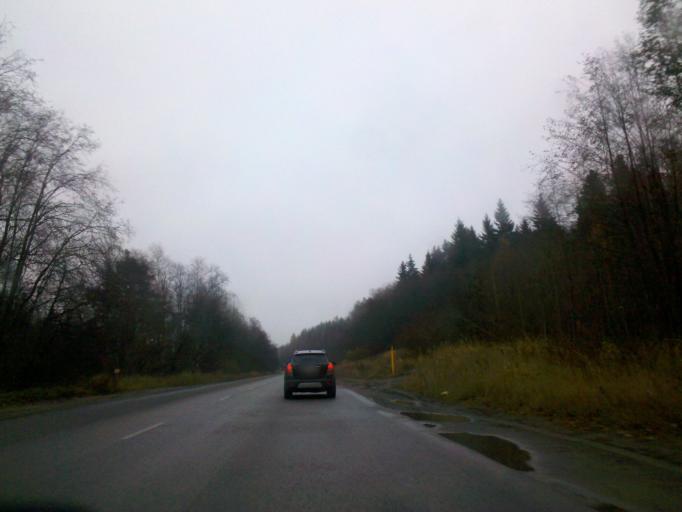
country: RU
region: Republic of Karelia
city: Petrozavodsk
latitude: 61.8206
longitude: 34.2491
